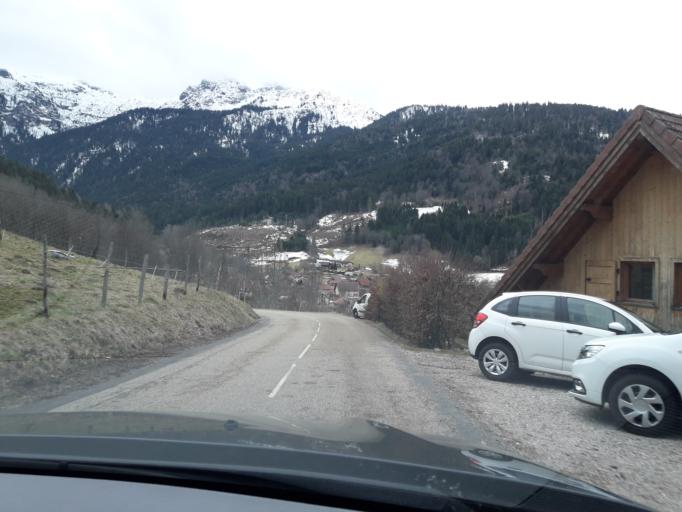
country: FR
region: Rhone-Alpes
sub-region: Departement de l'Isere
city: Le Champ-pres-Froges
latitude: 45.2432
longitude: 5.9744
